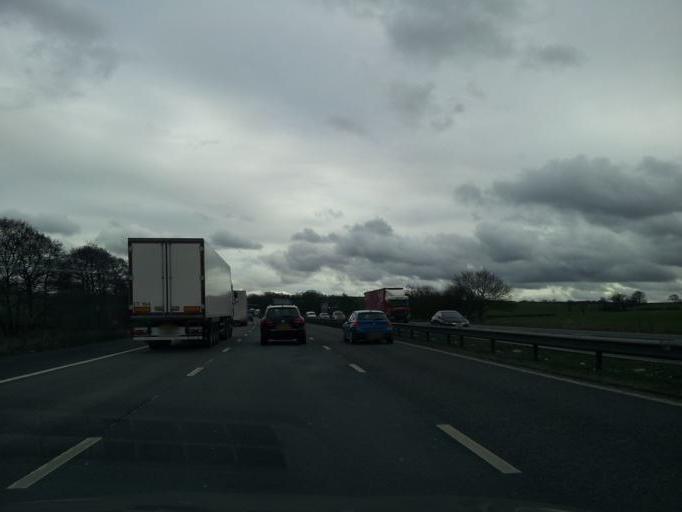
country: GB
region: England
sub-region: Staffordshire
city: Audley
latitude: 53.0001
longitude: -2.3217
